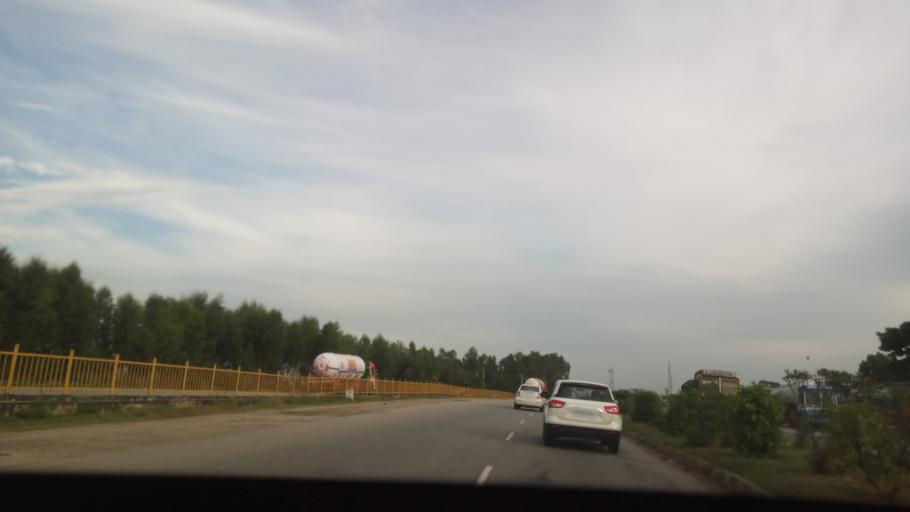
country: IN
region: Karnataka
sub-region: Ramanagara
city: Magadi
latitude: 13.0716
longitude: 77.2342
